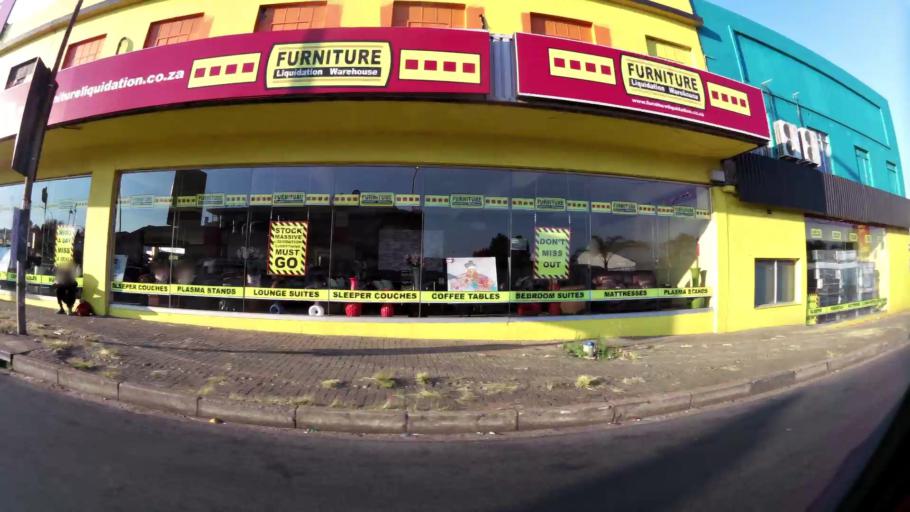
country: ZA
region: Gauteng
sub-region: City of Johannesburg Metropolitan Municipality
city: Johannesburg
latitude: -26.2158
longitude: 28.0093
